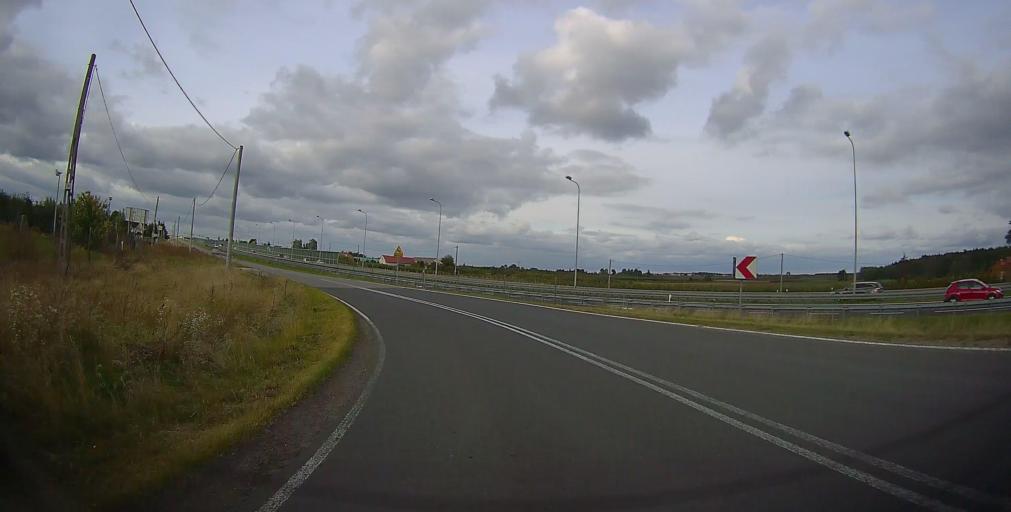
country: PL
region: Masovian Voivodeship
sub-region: Powiat bialobrzeski
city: Promna
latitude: 51.6999
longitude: 20.9326
